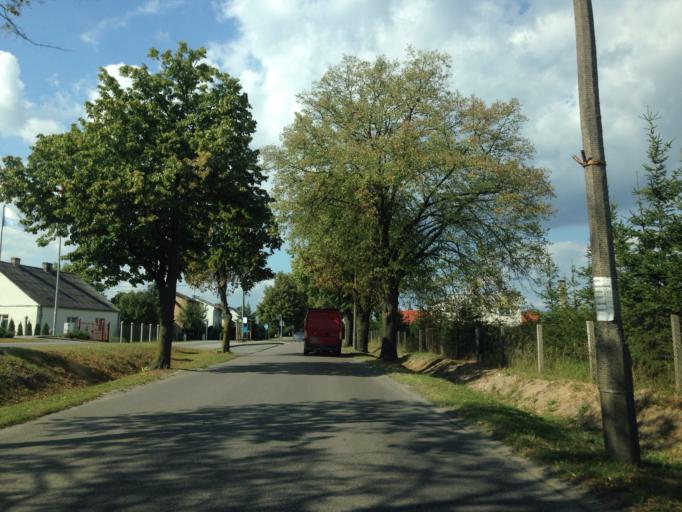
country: PL
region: Warmian-Masurian Voivodeship
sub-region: Powiat ilawski
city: Ilawa
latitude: 53.6115
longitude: 19.5702
